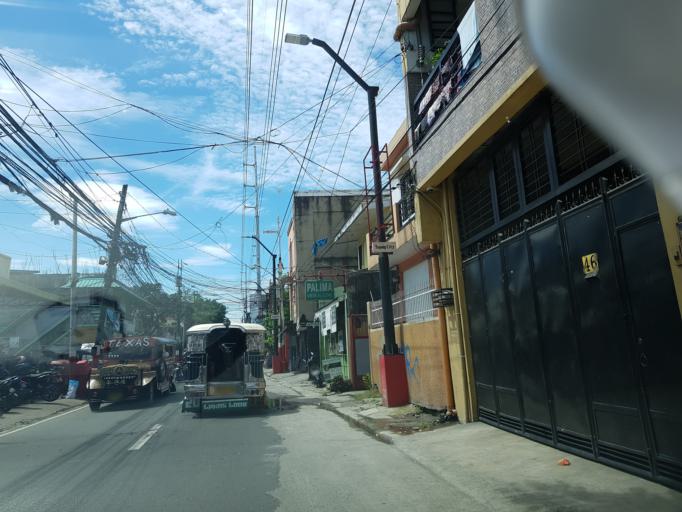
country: PH
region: Calabarzon
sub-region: Province of Rizal
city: Taguig
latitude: 14.5230
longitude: 121.0737
